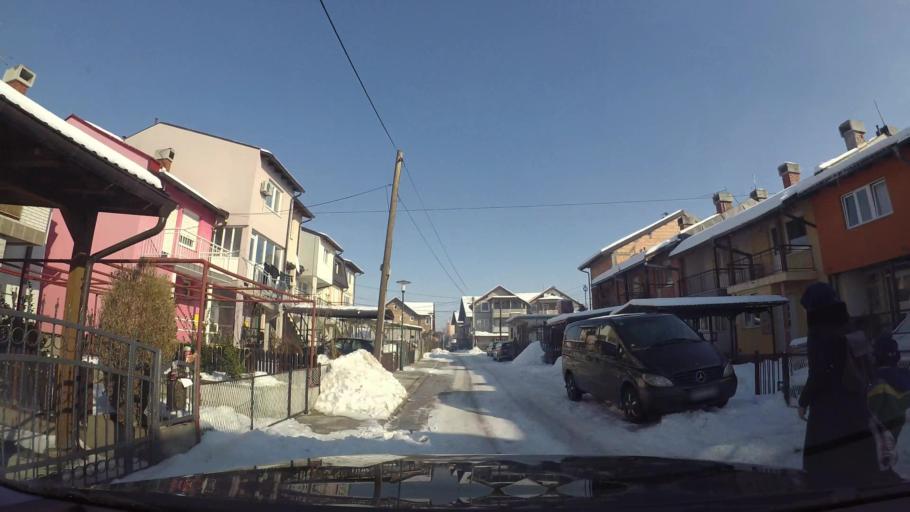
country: BA
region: Federation of Bosnia and Herzegovina
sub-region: Kanton Sarajevo
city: Sarajevo
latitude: 43.8145
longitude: 18.3184
